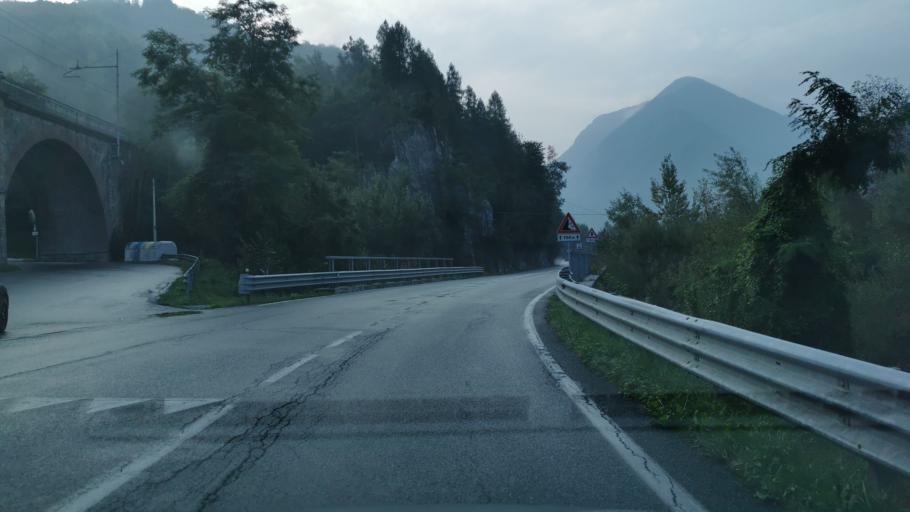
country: IT
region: Piedmont
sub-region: Provincia di Cuneo
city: Vernante
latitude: 44.2548
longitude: 7.5282
